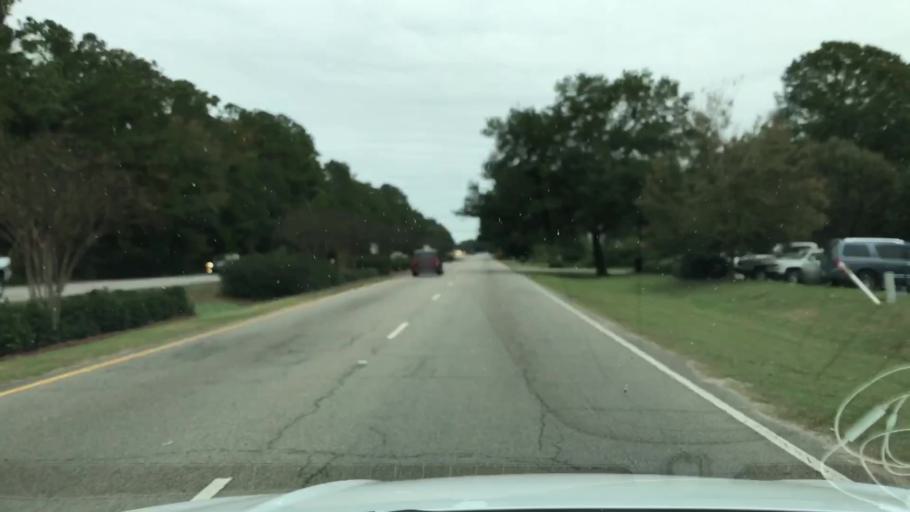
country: US
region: South Carolina
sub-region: Georgetown County
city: Murrells Inlet
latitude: 33.4931
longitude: -79.0887
